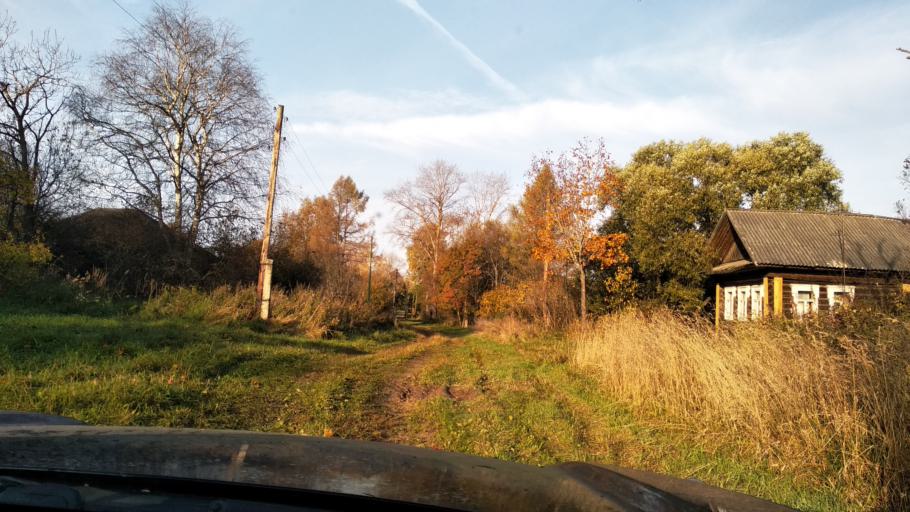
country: RU
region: Tverskaya
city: Krasnyy Kholm
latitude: 58.0094
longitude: 37.1964
